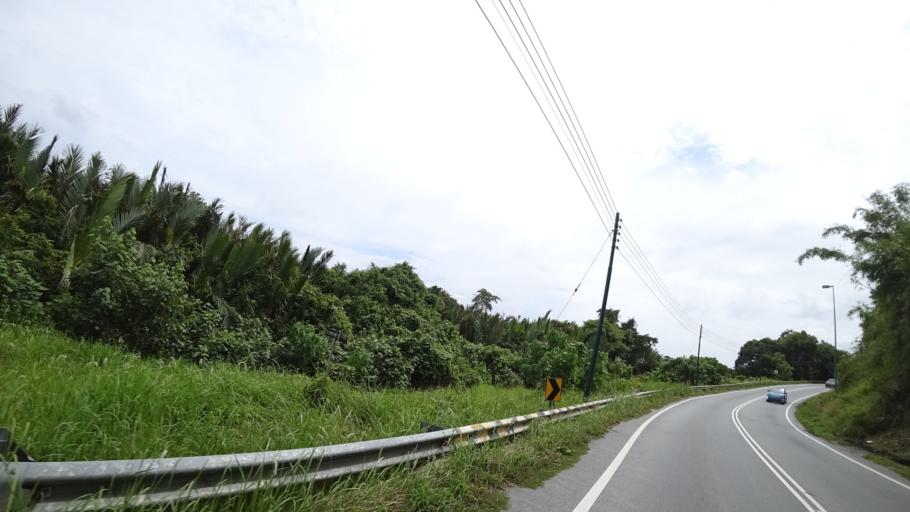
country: BN
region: Tutong
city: Tutong
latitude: 4.8041
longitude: 114.6715
